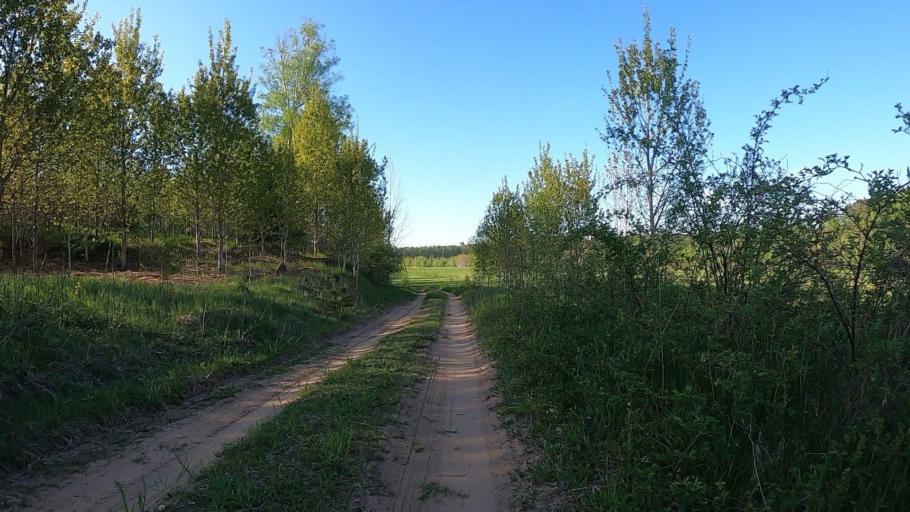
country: LV
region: Baldone
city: Baldone
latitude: 56.7709
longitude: 24.3287
